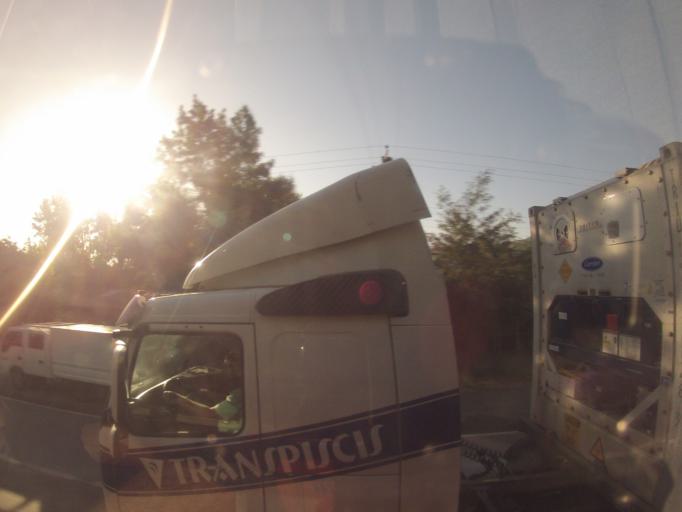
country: CL
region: O'Higgins
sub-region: Provincia de Colchagua
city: Chimbarongo
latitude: -34.7102
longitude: -71.0286
